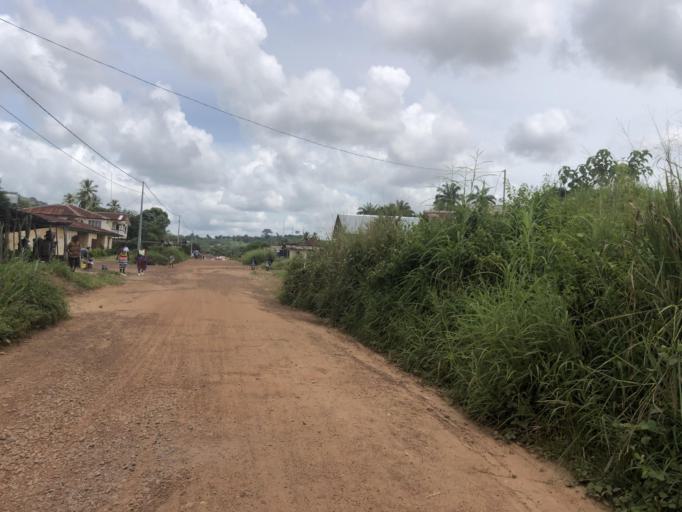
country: SL
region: Northern Province
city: Makeni
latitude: 8.8603
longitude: -12.0556
